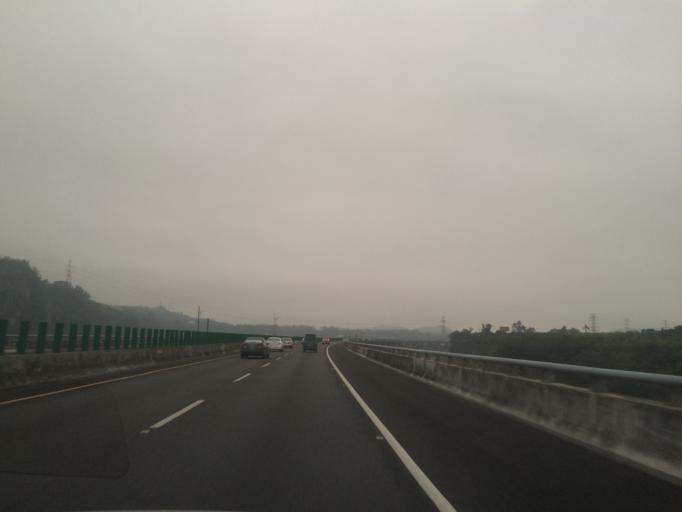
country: TW
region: Taiwan
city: Zhongxing New Village
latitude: 23.9823
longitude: 120.7678
